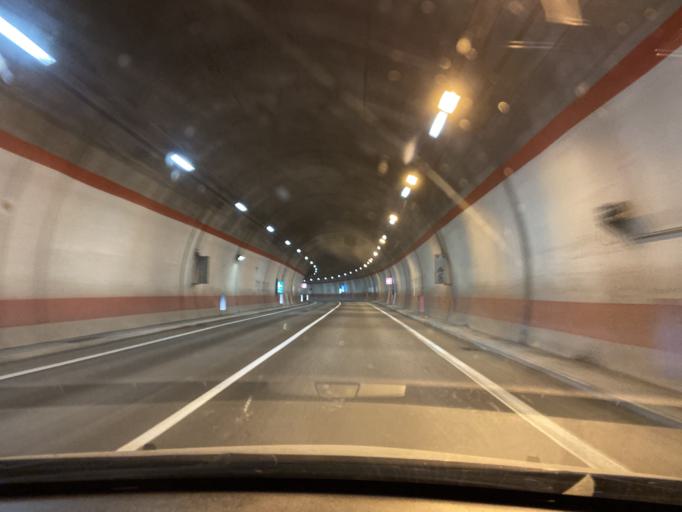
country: IT
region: Piedmont
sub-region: Provincia di Torino
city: Cesana Torinese
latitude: 44.9513
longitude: 6.7743
